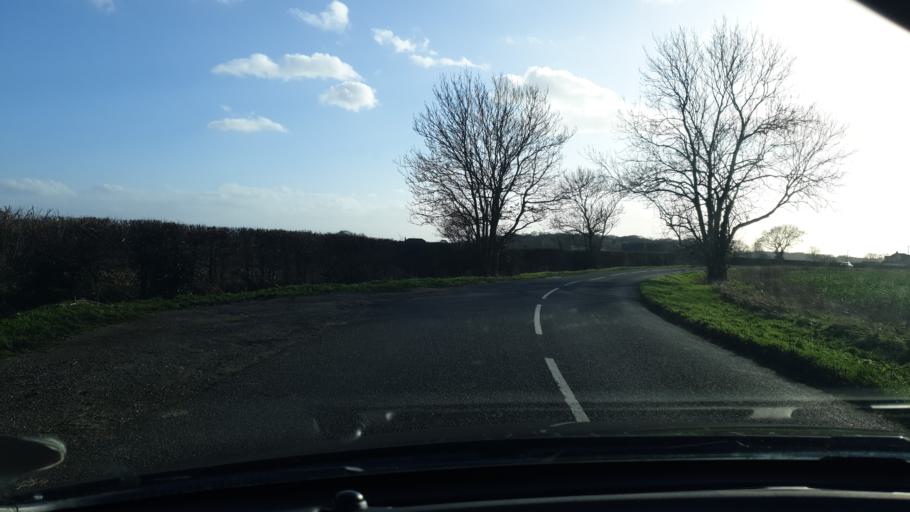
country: GB
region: England
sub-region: Essex
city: Mistley
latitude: 51.9019
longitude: 1.1432
